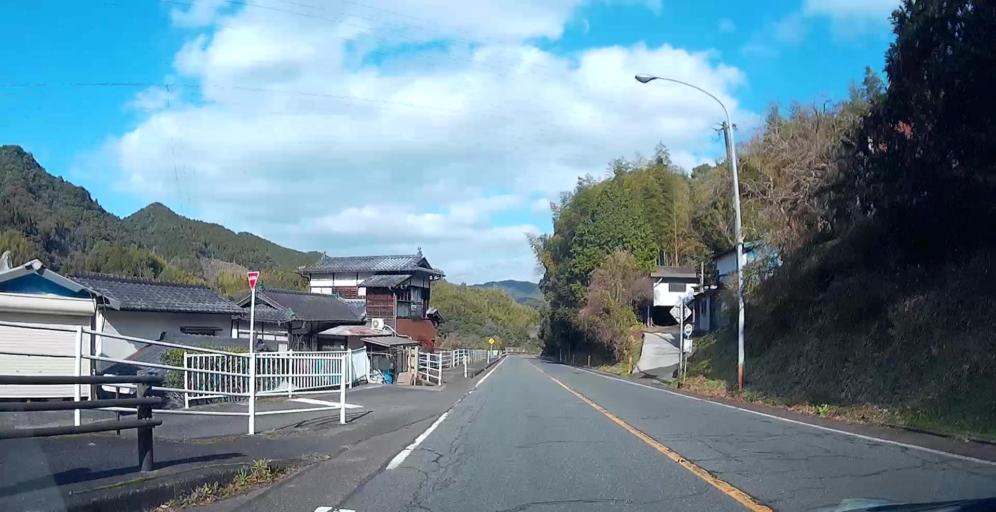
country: JP
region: Kumamoto
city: Yatsushiro
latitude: 32.3934
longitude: 130.5451
